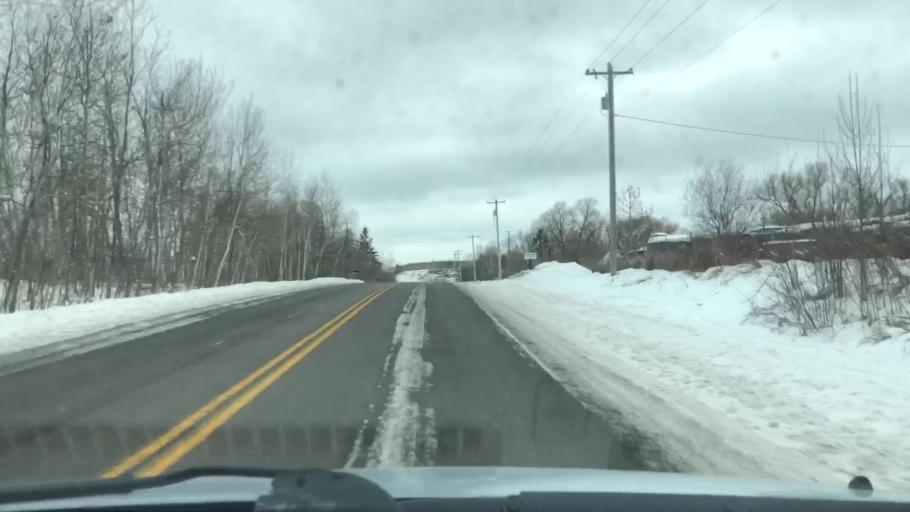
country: US
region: Minnesota
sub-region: Carlton County
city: Esko
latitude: 46.7024
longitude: -92.2873
